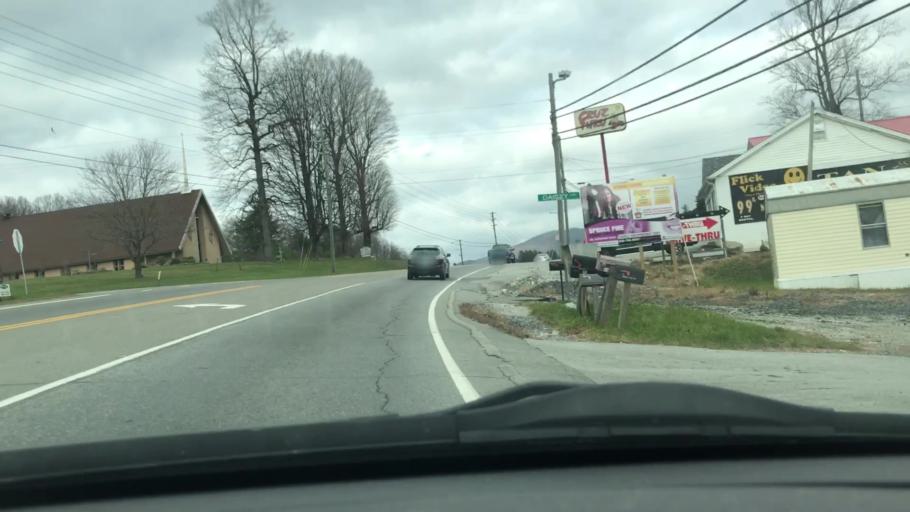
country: US
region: North Carolina
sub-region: Mitchell County
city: Spruce Pine
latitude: 35.9018
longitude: -82.0742
